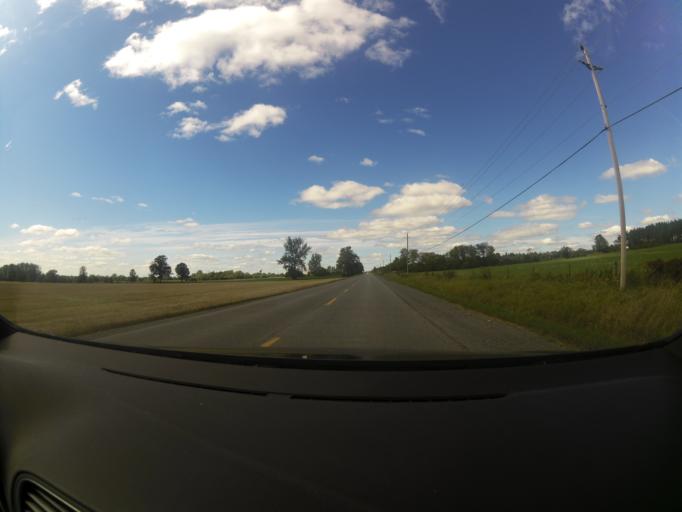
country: CA
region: Ontario
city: Carleton Place
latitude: 45.2193
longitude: -76.1569
